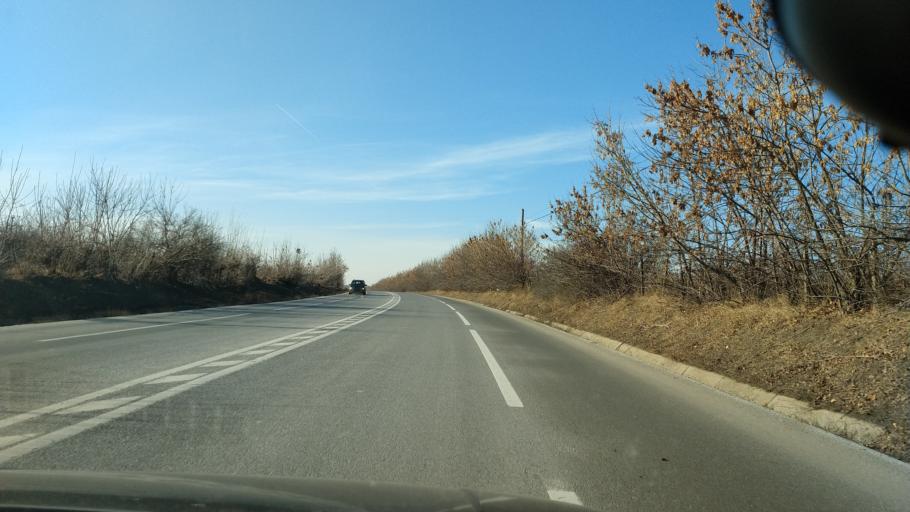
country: RO
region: Iasi
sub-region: Comuna Baltati
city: Baltati
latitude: 47.2233
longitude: 27.1648
